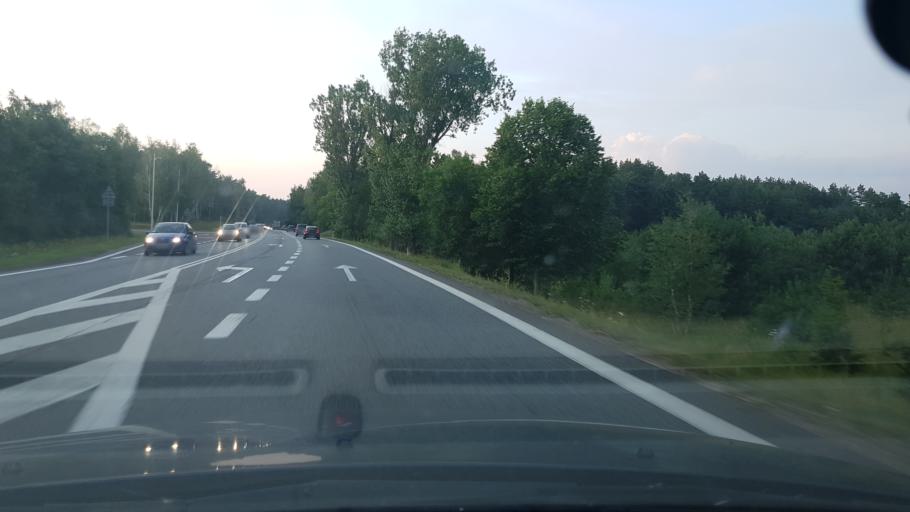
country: PL
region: Masovian Voivodeship
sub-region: Powiat mlawski
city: Mlawa
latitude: 53.1317
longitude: 20.3952
